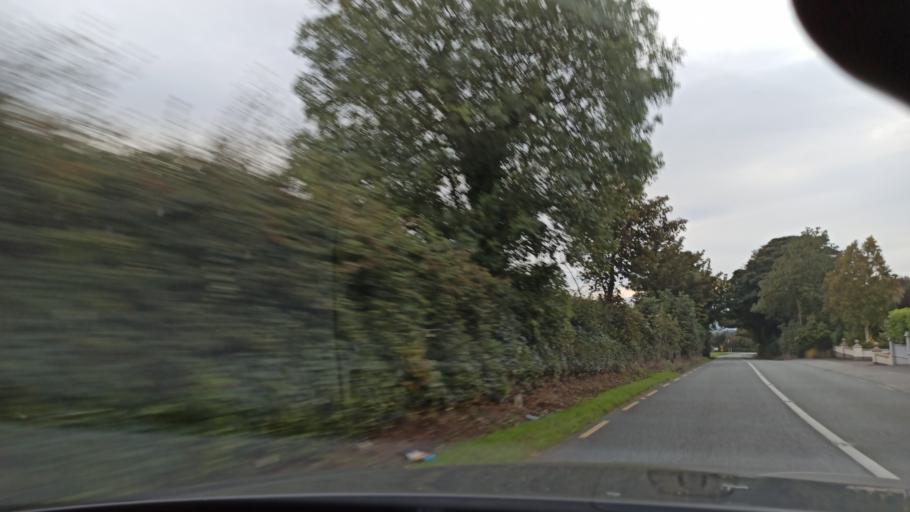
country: IE
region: Munster
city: Cashel
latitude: 52.4726
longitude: -7.8365
